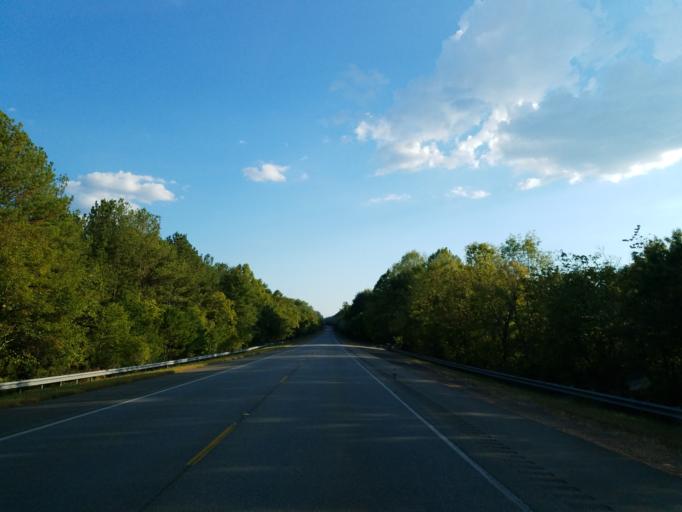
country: US
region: Georgia
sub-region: Murray County
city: Chatsworth
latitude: 34.6257
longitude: -84.7139
